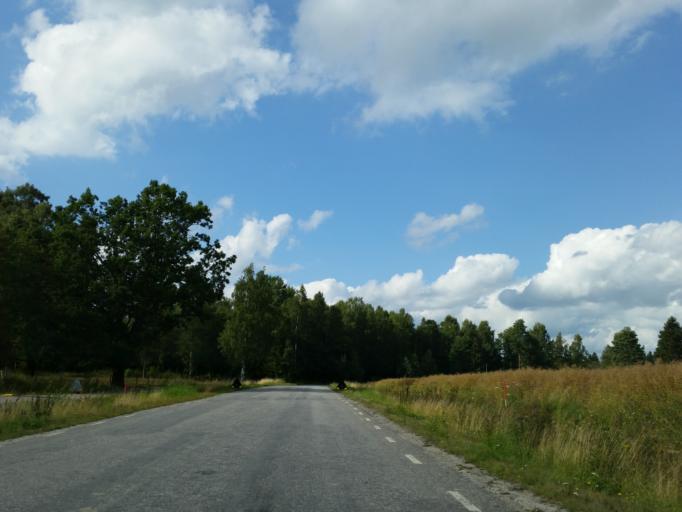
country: SE
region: Soedermanland
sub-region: Strangnas Kommun
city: Mariefred
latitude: 59.2200
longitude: 17.2955
